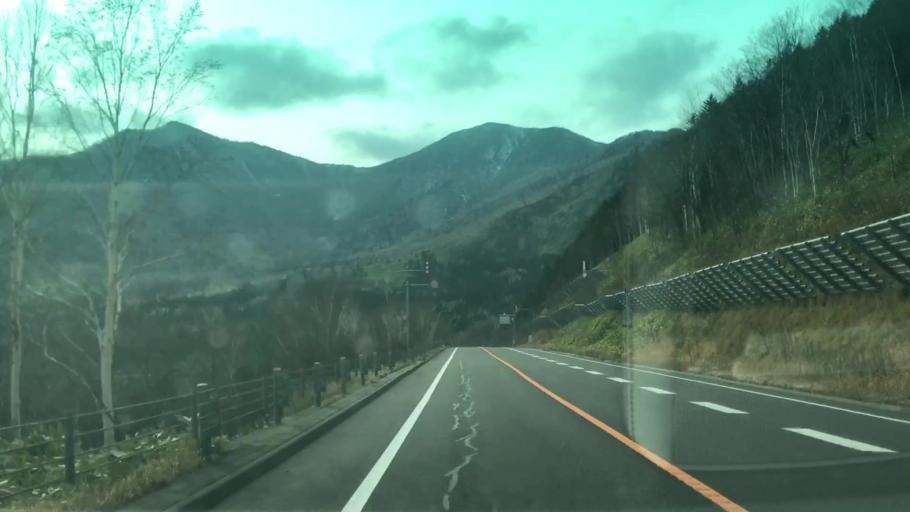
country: JP
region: Hokkaido
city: Otofuke
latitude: 42.9646
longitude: 142.7926
